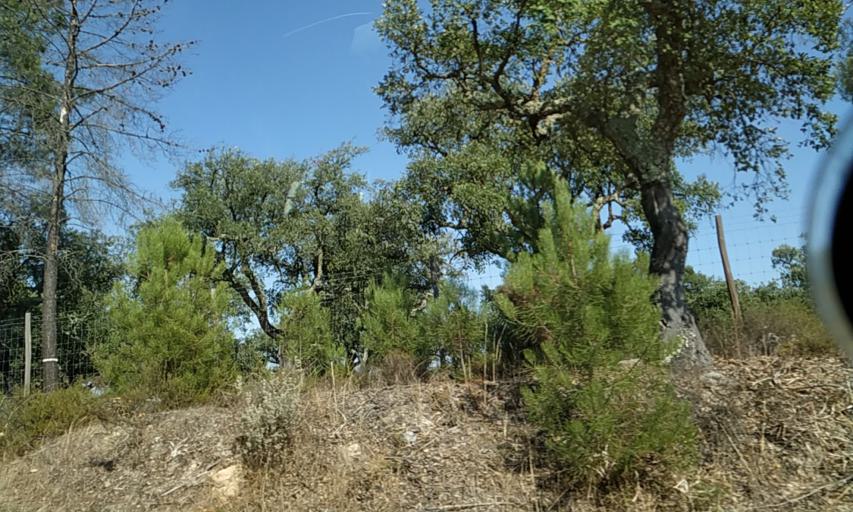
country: PT
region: Santarem
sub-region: Coruche
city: Coruche
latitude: 38.8112
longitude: -8.5763
